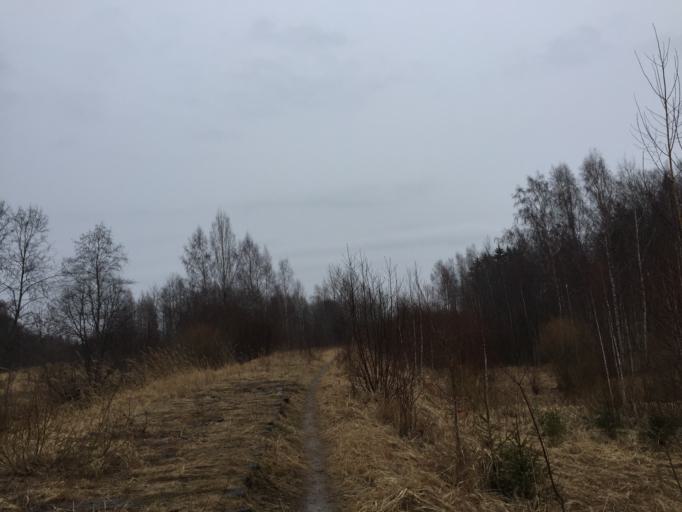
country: LV
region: Lielvarde
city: Lielvarde
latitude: 56.7311
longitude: 24.7774
